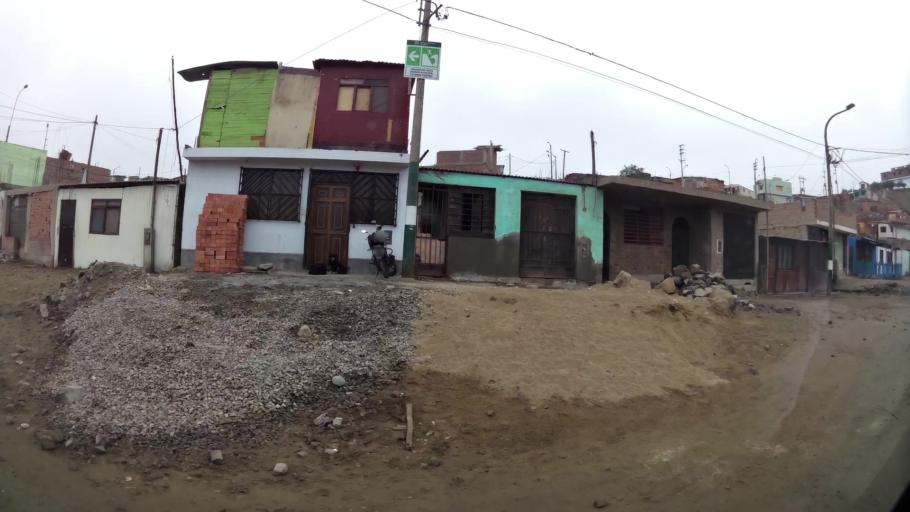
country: PE
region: Lima
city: Ventanilla
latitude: -11.8799
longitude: -77.1356
